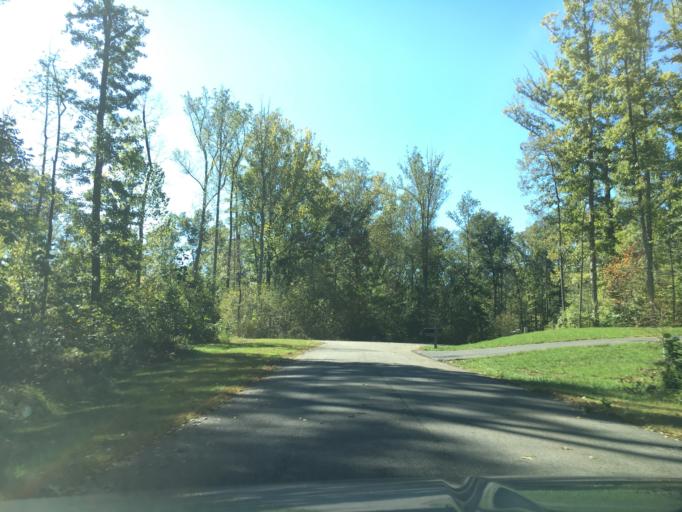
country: US
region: Virginia
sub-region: Goochland County
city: Goochland
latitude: 37.6981
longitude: -77.8375
